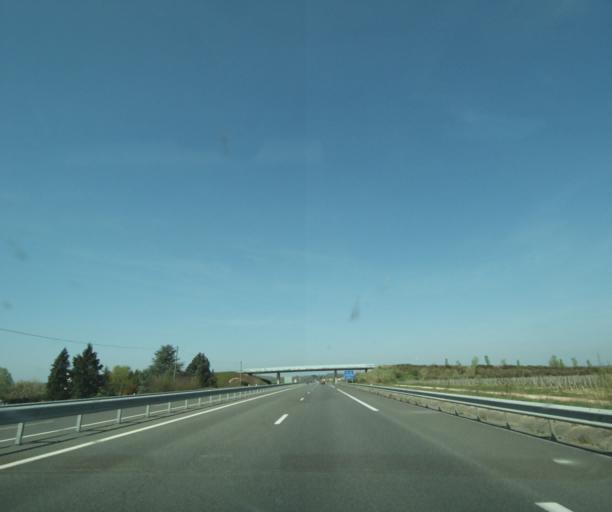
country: FR
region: Bourgogne
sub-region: Departement de la Nievre
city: Pouilly-sur-Loire
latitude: 47.3226
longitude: 2.9346
